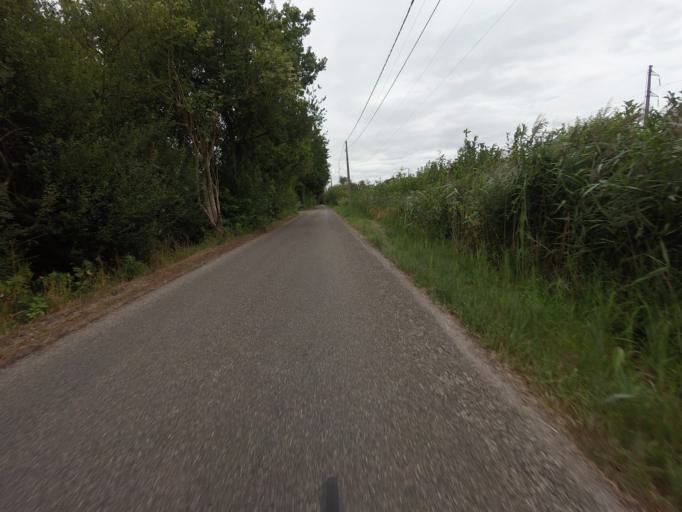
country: BE
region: Flanders
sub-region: Provincie Antwerpen
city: Schoten
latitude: 51.2821
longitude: 4.5338
